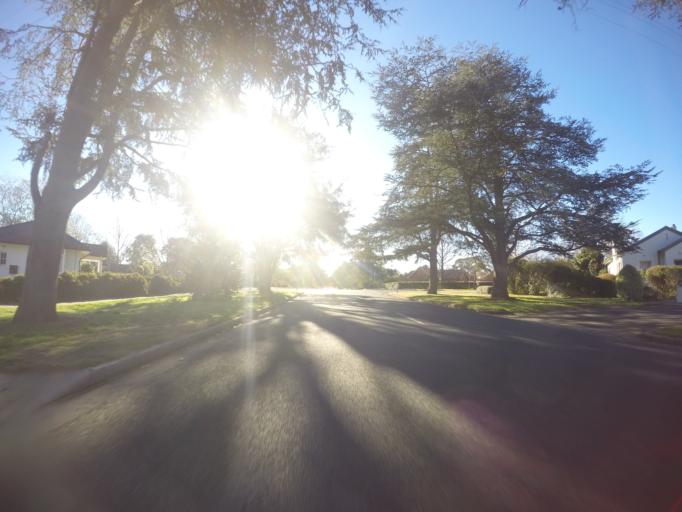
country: AU
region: Australian Capital Territory
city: Canberra
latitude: -35.2800
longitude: 149.1415
